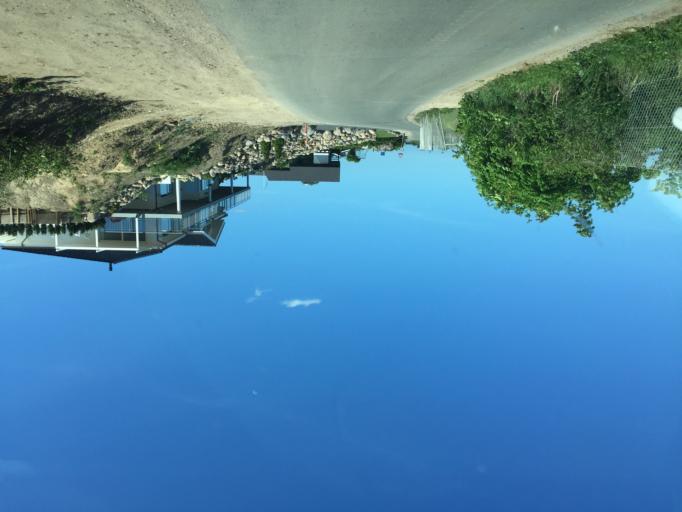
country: DK
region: Zealand
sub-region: Stevns Kommune
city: Stroby Egede
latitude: 55.4085
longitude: 12.2761
